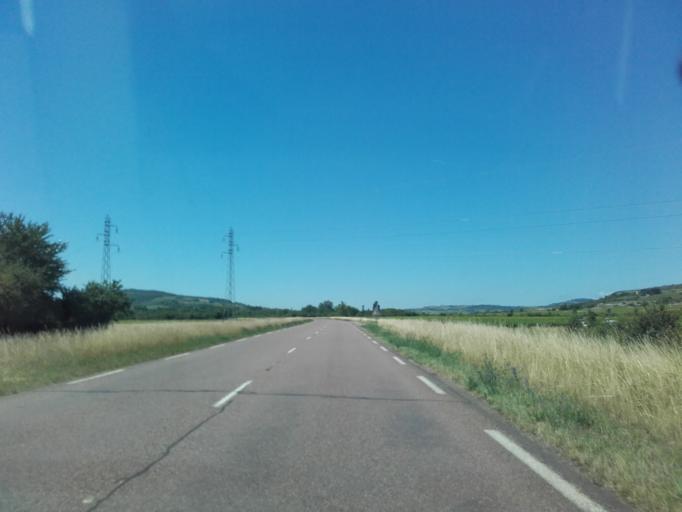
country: FR
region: Bourgogne
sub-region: Departement de la Cote-d'Or
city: Corpeau
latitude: 46.9210
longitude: 4.7332
